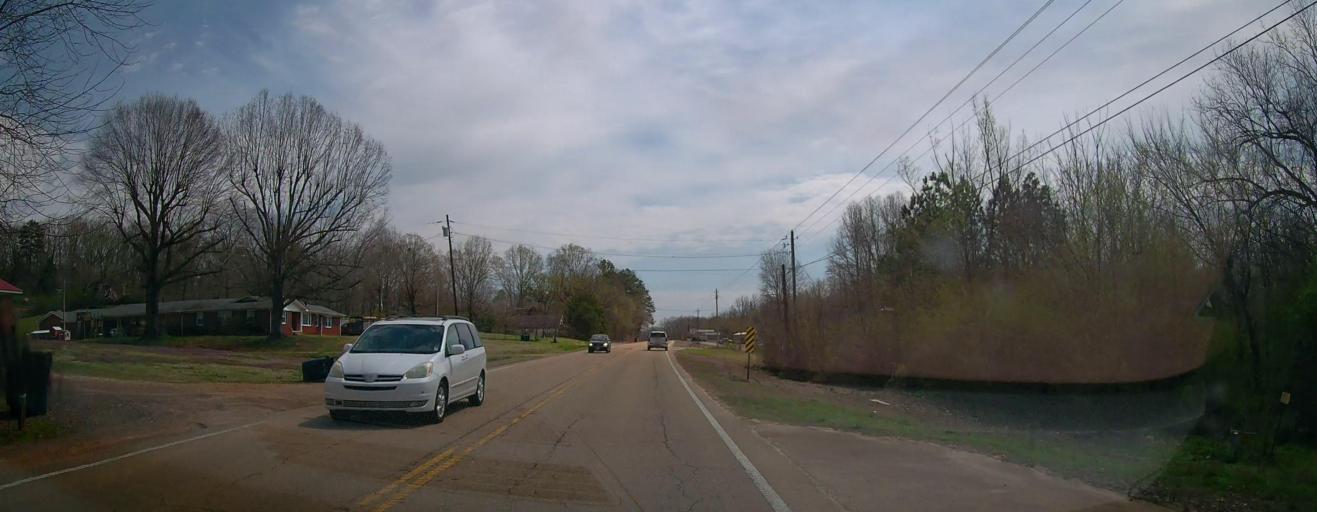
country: US
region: Mississippi
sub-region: Marshall County
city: Holly Springs
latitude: 34.6319
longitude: -89.2746
